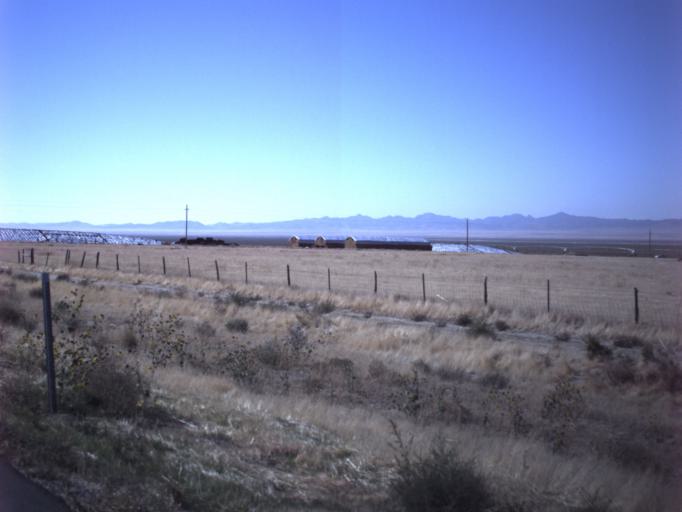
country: US
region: Utah
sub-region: Tooele County
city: Grantsville
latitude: 40.5249
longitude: -112.7477
